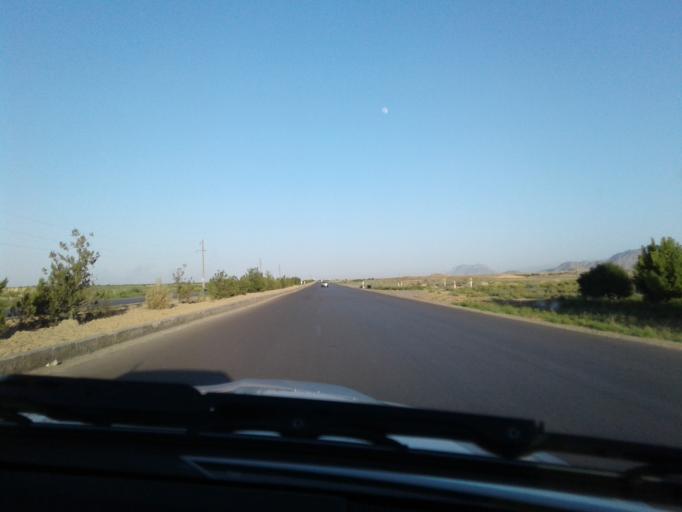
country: TM
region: Ahal
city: Baharly
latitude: 38.2463
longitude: 57.7552
